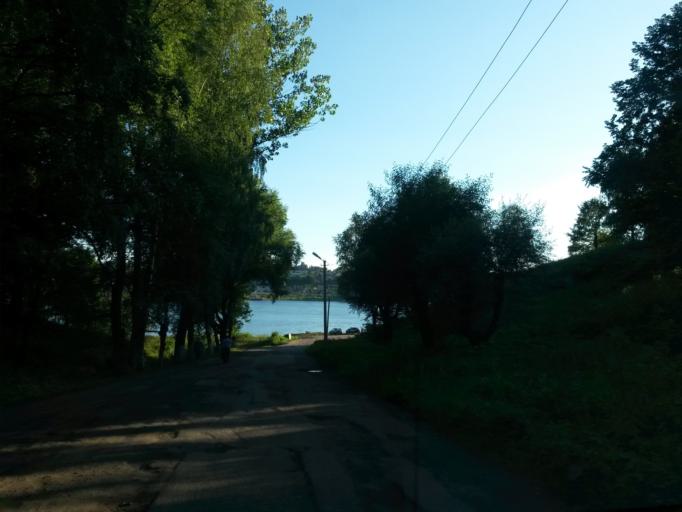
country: RU
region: Jaroslavl
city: Tutayev
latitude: 57.8785
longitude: 39.5431
